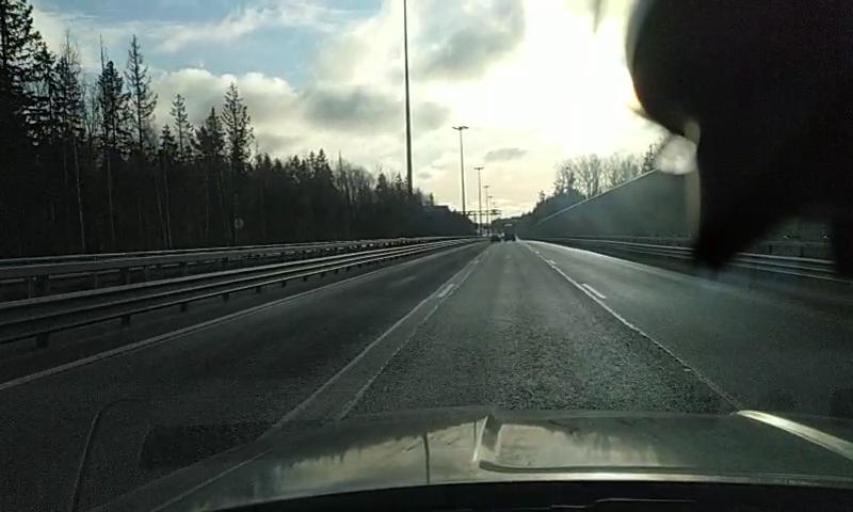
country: RU
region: St.-Petersburg
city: Beloostrov
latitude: 60.1254
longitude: 30.0679
